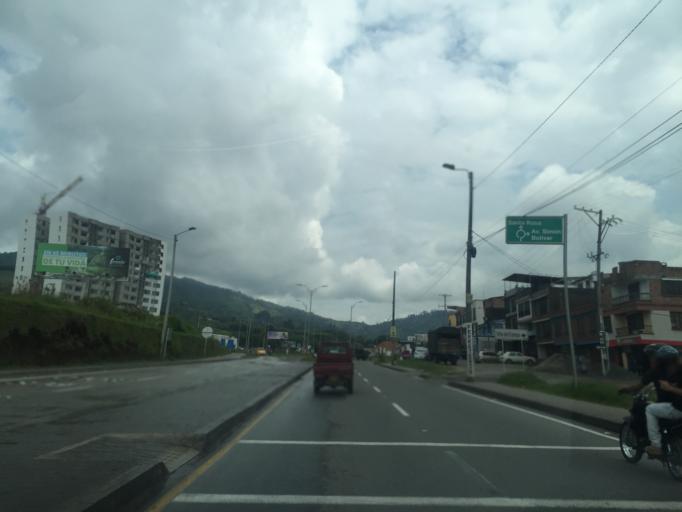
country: CO
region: Risaralda
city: Dos Quebradas
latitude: 4.8438
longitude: -75.6716
